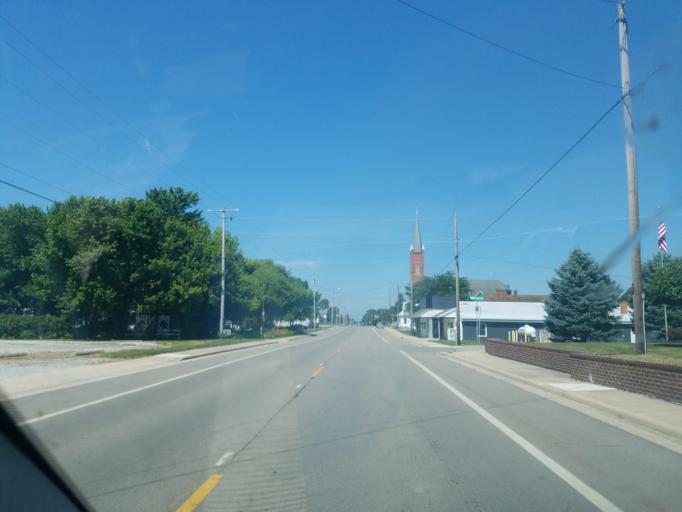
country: US
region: Ohio
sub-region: Auglaize County
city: New Bremen
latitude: 40.4076
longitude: -84.4704
